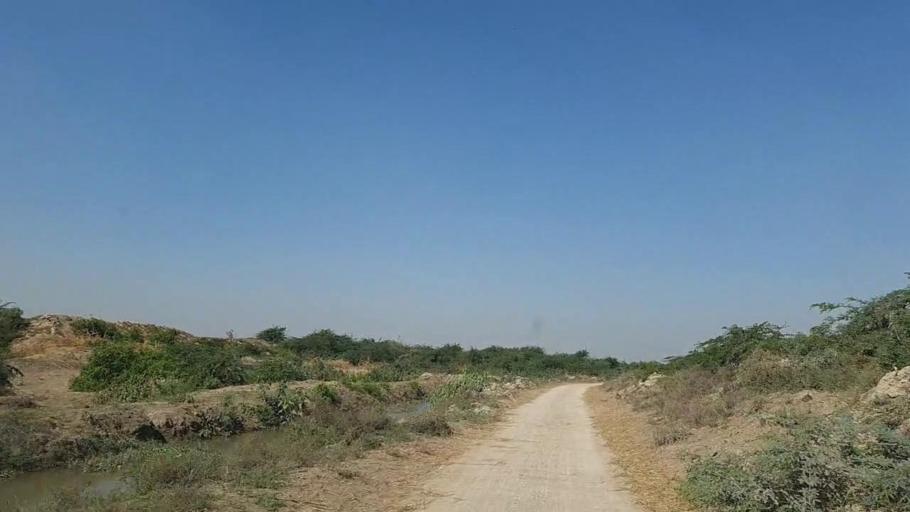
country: PK
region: Sindh
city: Daro Mehar
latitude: 24.7637
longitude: 68.1556
